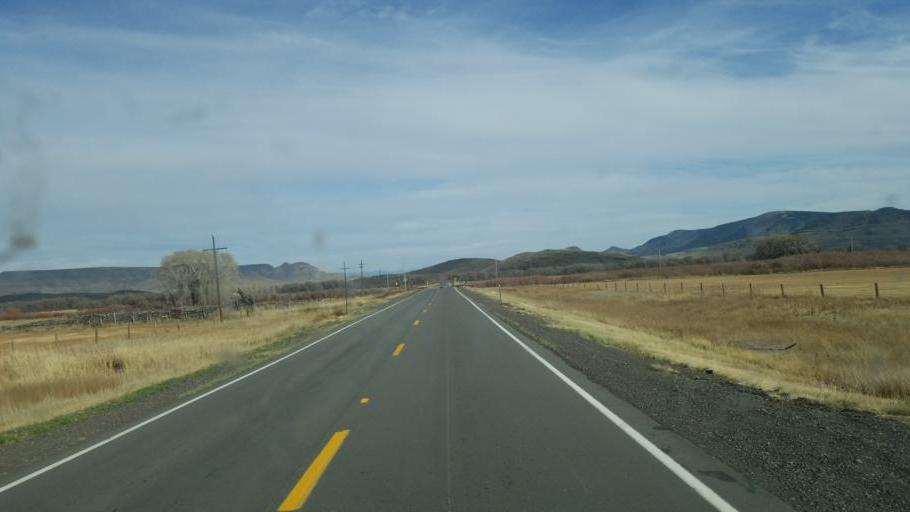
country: US
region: Colorado
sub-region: Conejos County
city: Conejos
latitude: 37.1737
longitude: -105.9133
